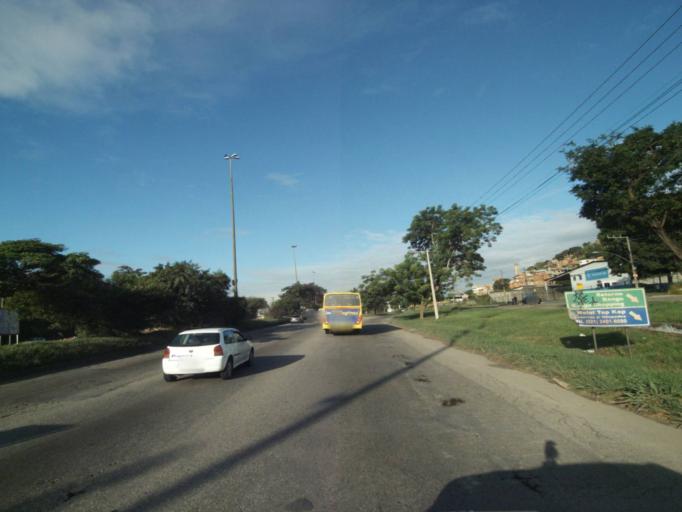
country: BR
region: Rio de Janeiro
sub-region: Nilopolis
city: Nilopolis
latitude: -22.8565
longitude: -43.4768
